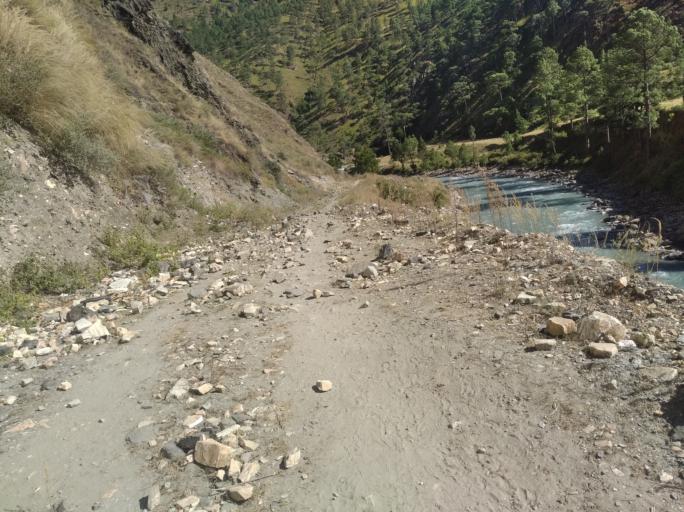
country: NP
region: Mid Western
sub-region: Karnali Zone
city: Jumla
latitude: 28.9346
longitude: 82.9115
